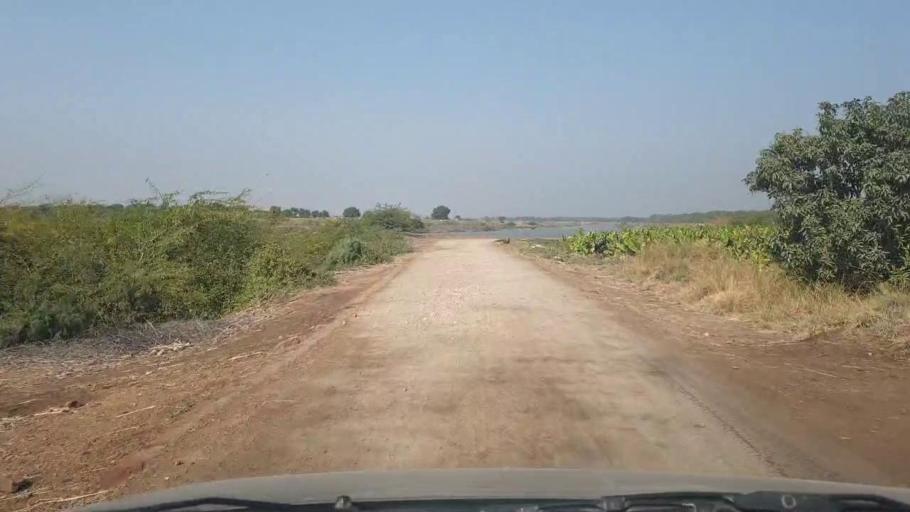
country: PK
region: Sindh
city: Mirwah Gorchani
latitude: 25.2507
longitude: 69.1029
